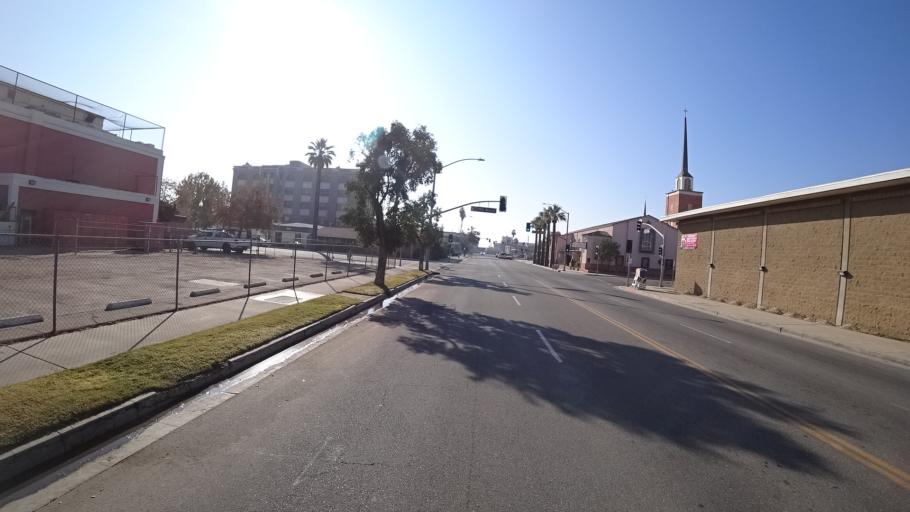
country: US
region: California
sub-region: Kern County
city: Bakersfield
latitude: 35.3747
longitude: -119.0212
